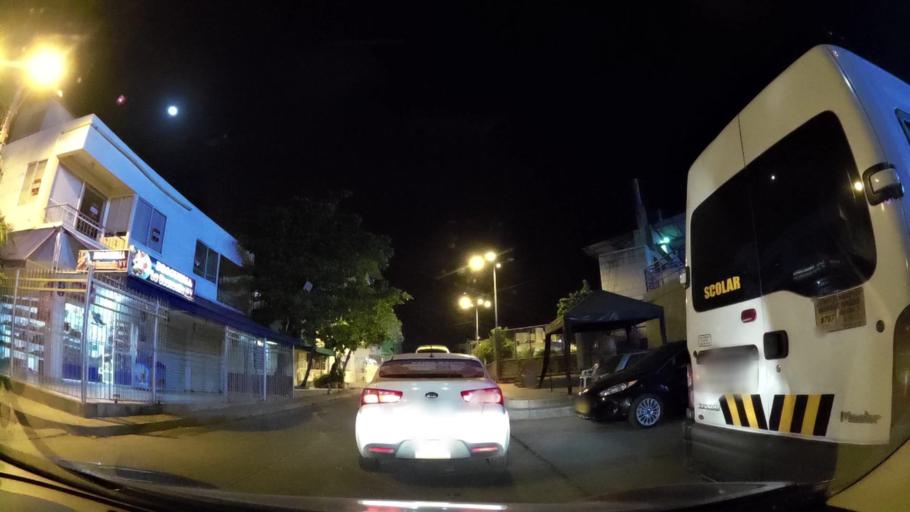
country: CO
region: Bolivar
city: Cartagena
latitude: 10.3803
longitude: -75.4978
